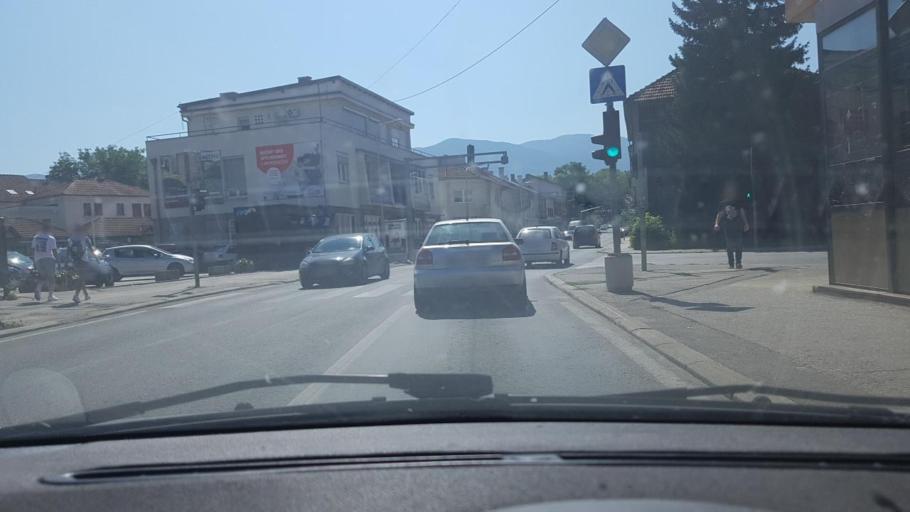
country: BA
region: Federation of Bosnia and Herzegovina
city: Bihac
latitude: 44.8142
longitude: 15.8754
